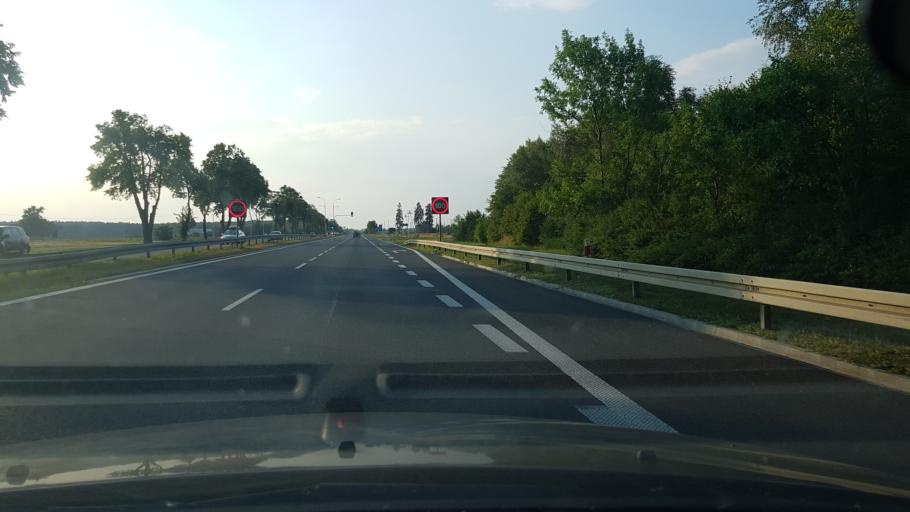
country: PL
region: Masovian Voivodeship
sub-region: Powiat plonski
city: Zaluski
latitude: 52.4853
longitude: 20.5501
